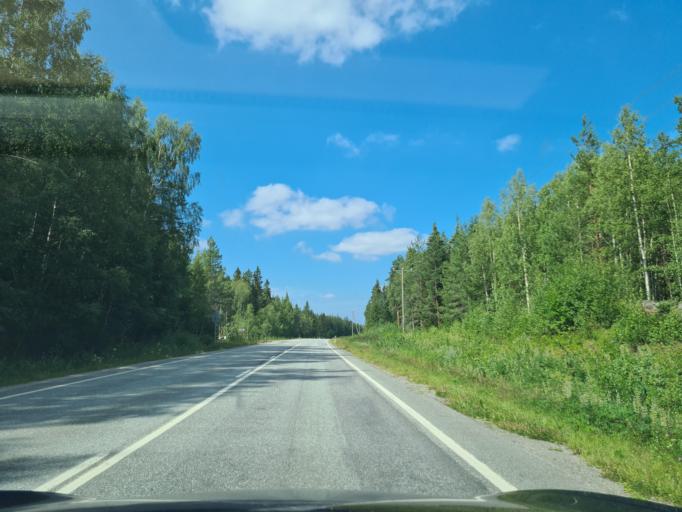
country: FI
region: Ostrobothnia
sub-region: Vaasa
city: Vaasa
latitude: 63.1817
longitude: 21.5712
